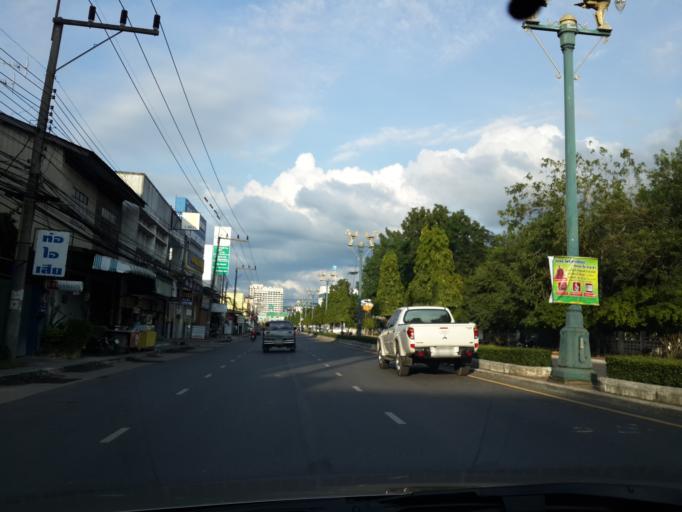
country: TH
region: Yala
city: Yala
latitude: 6.5510
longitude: 101.2802
